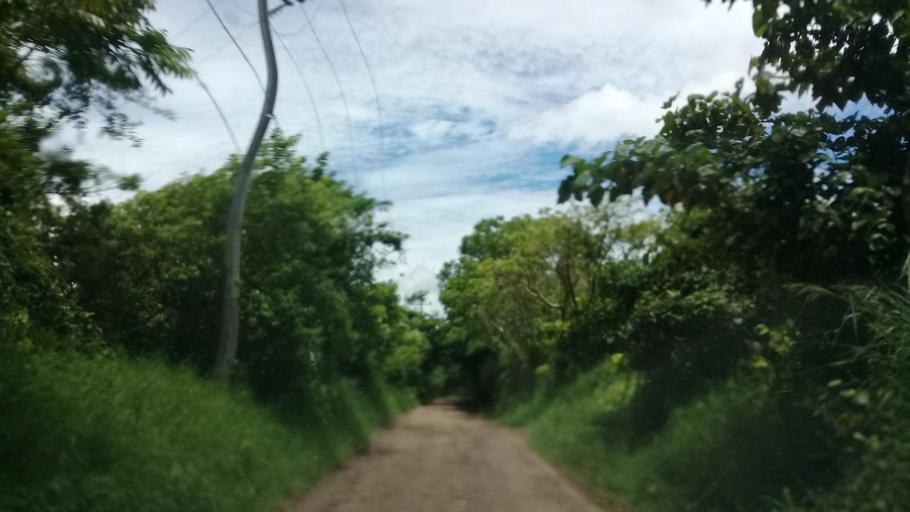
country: MX
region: Veracruz
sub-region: Naolinco
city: El Espinal
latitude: 19.5890
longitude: -96.8659
